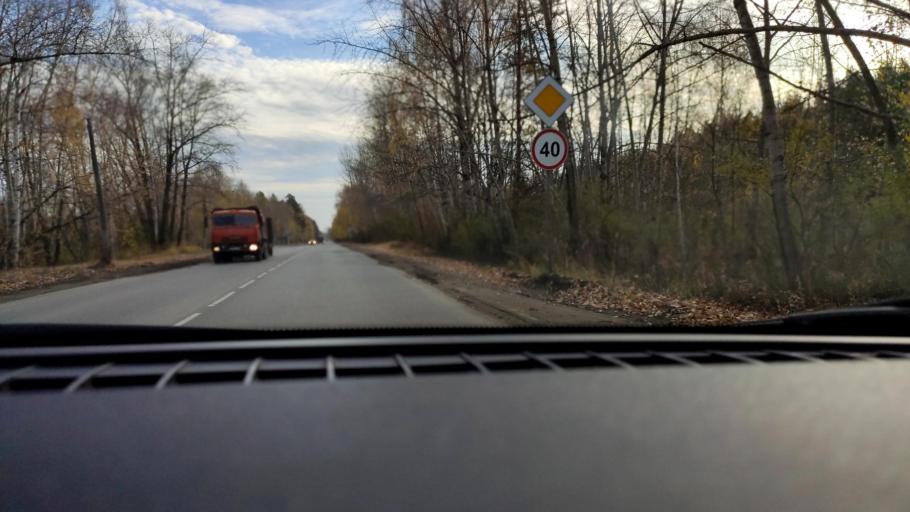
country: RU
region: Perm
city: Overyata
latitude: 58.0148
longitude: 55.9035
